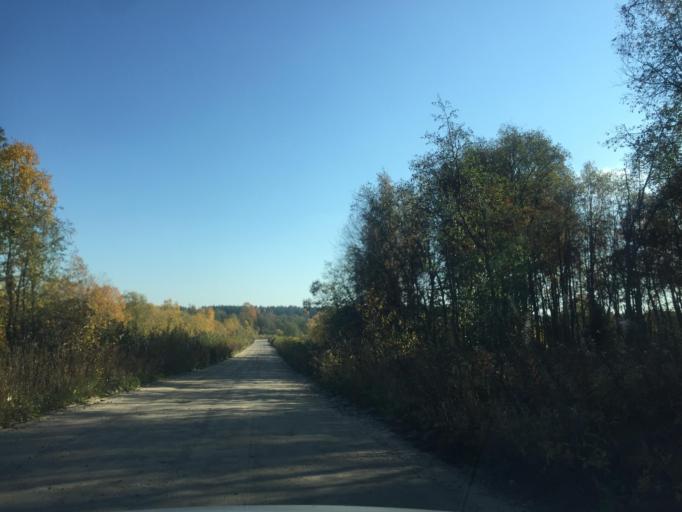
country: RU
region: Leningrad
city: Kuznechnoye
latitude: 61.2967
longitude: 30.0615
